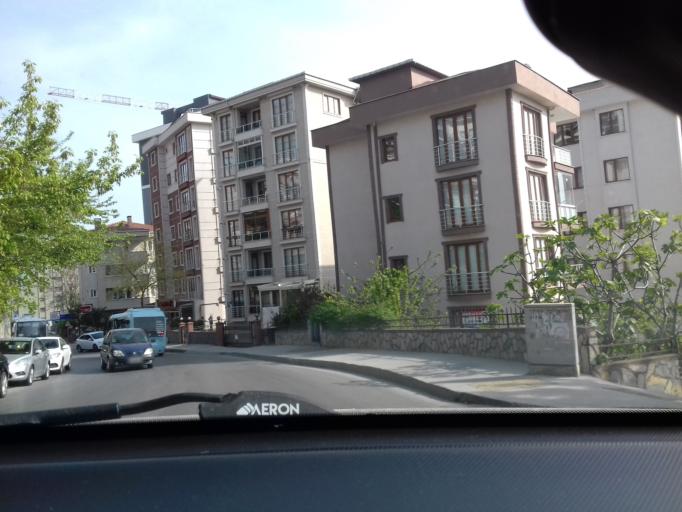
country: TR
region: Istanbul
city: Pendik
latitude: 40.9105
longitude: 29.2337
